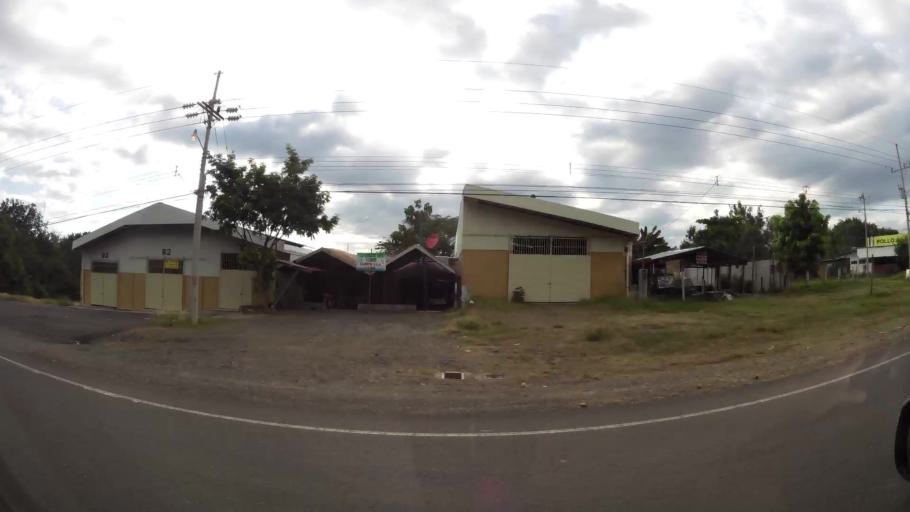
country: CR
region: Alajuela
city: Orotina
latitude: 9.8756
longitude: -84.5740
